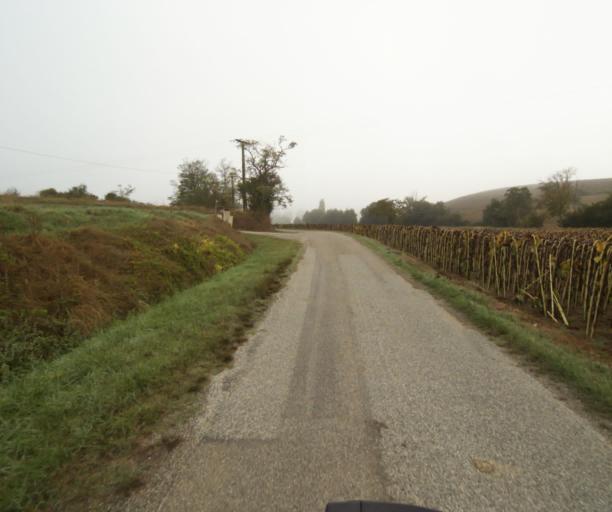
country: FR
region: Midi-Pyrenees
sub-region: Departement du Tarn-et-Garonne
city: Nohic
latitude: 43.9294
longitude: 1.4842
